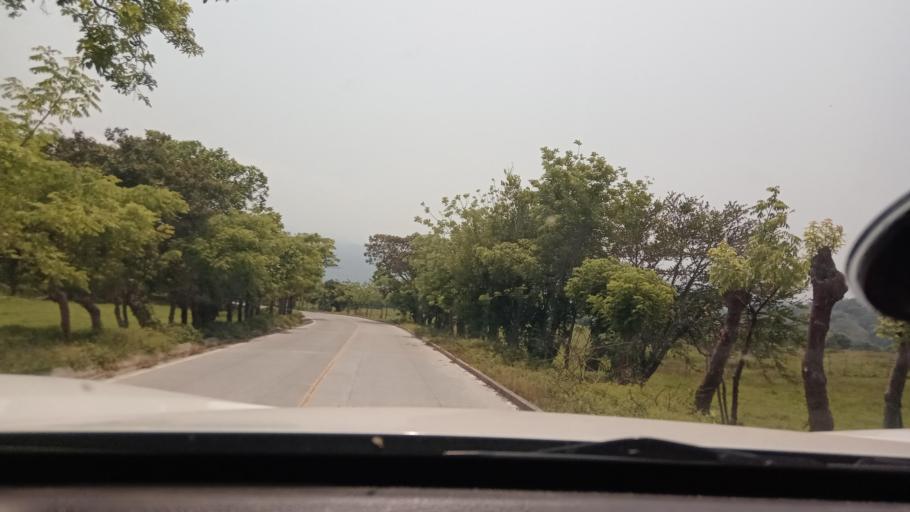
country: MX
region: Veracruz
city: Catemaco
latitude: 18.5613
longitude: -95.0360
